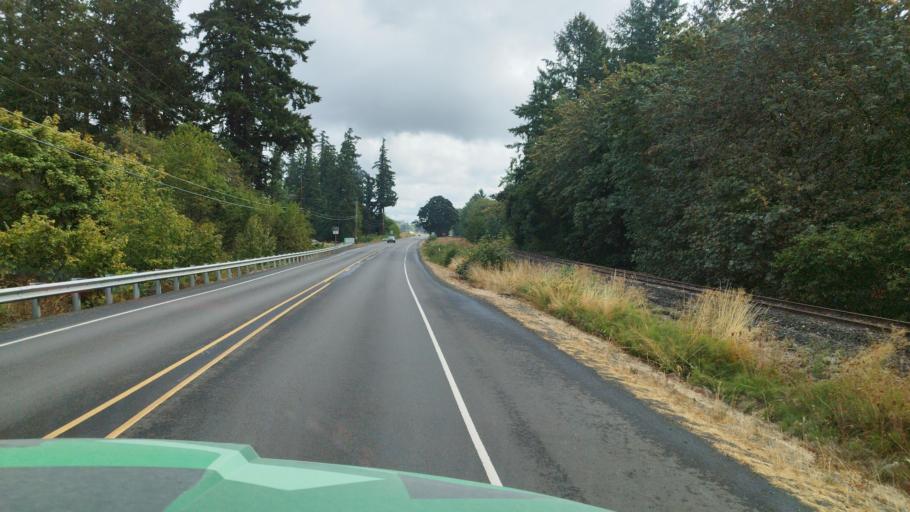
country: US
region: Oregon
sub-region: Yamhill County
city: Lafayette
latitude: 45.2420
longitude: -123.1031
